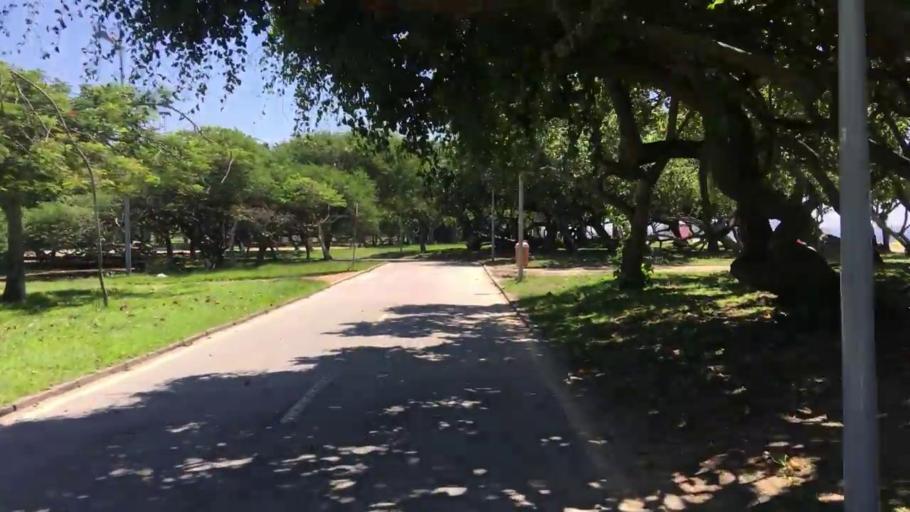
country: BR
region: Rio de Janeiro
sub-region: Rio De Janeiro
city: Rio de Janeiro
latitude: -22.9267
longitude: -43.1708
